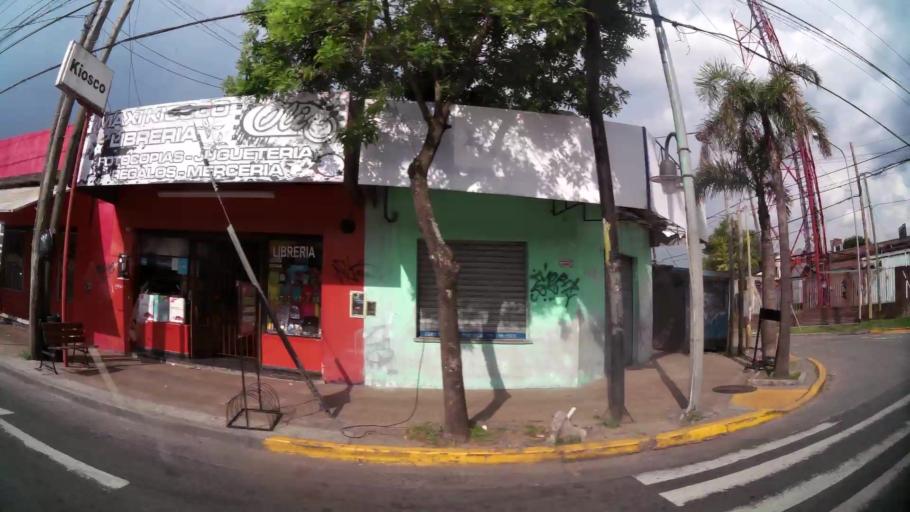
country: AR
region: Buenos Aires
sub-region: Partido de Tigre
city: Tigre
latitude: -34.4775
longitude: -58.6243
